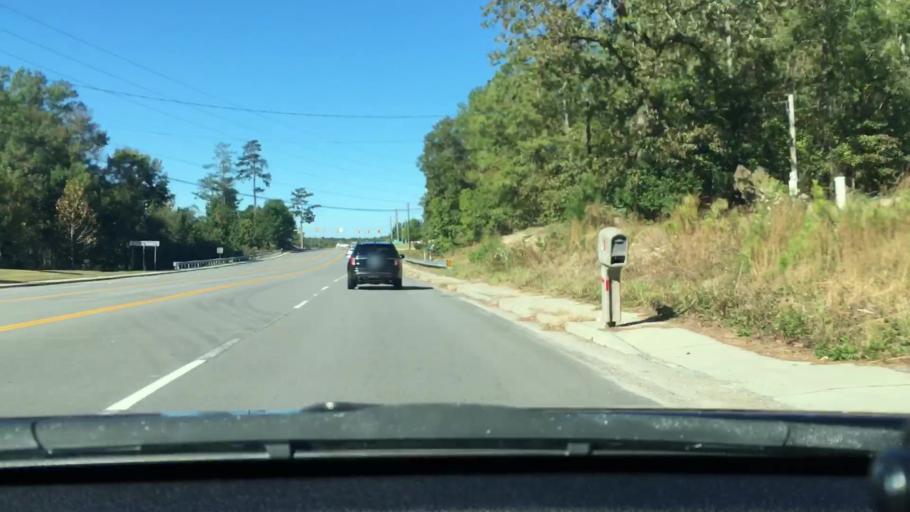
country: US
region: South Carolina
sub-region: Lexington County
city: Irmo
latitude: 34.0894
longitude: -81.1572
